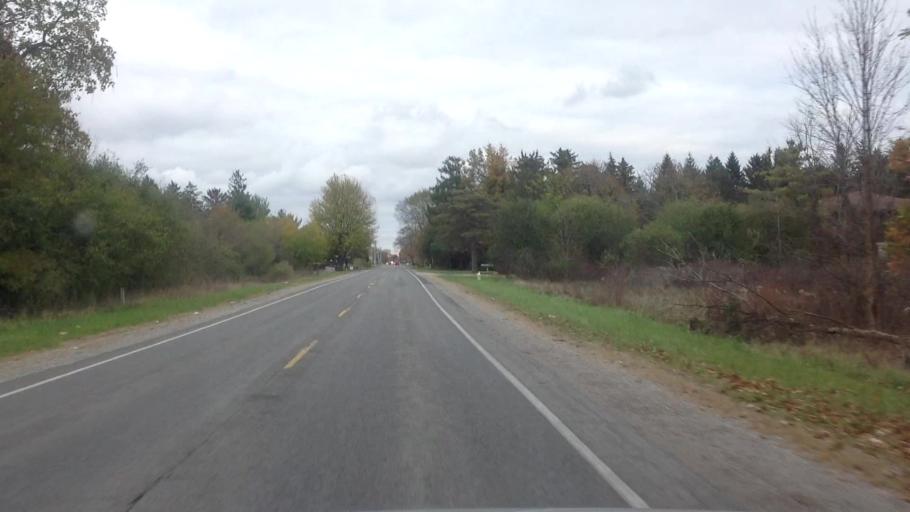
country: US
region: Michigan
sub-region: Saginaw County
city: Buena Vista
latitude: 43.3824
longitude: -83.9218
